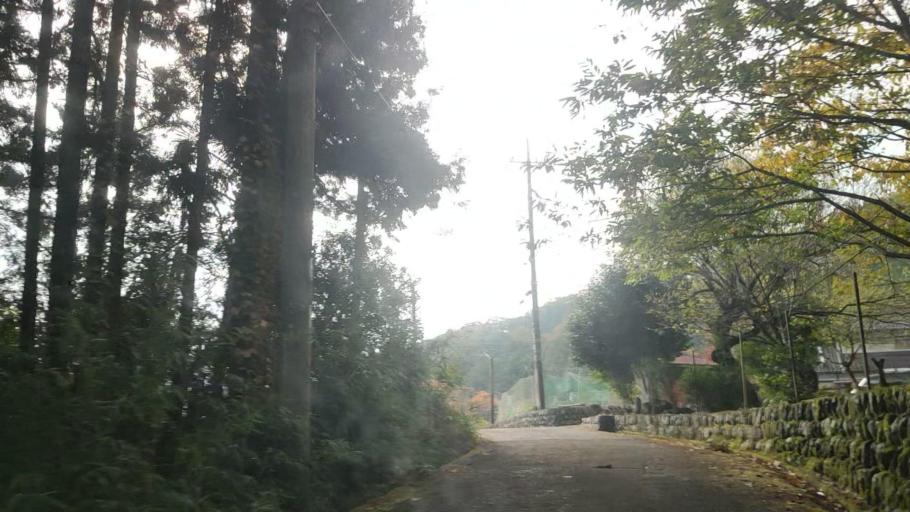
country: JP
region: Shizuoka
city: Fujinomiya
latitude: 35.3395
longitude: 138.4398
